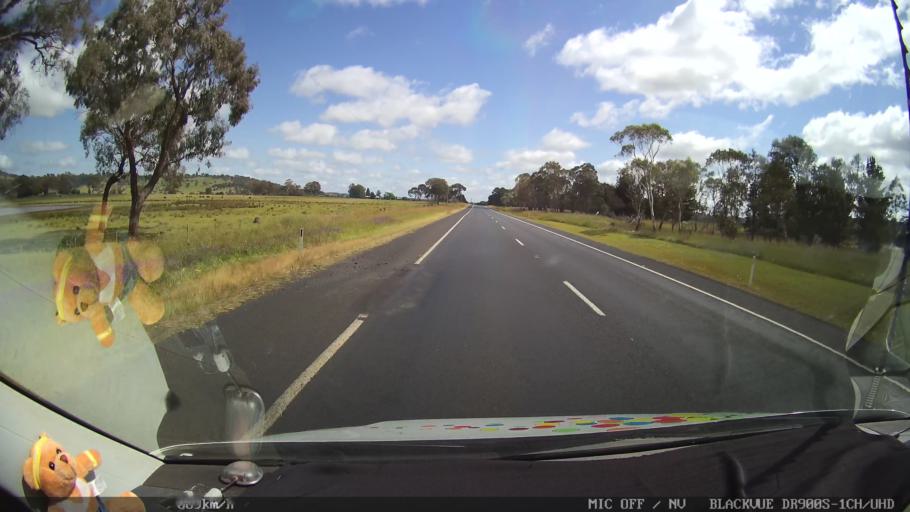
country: AU
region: New South Wales
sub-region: Glen Innes Severn
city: Glen Innes
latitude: -29.8735
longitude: 151.7350
